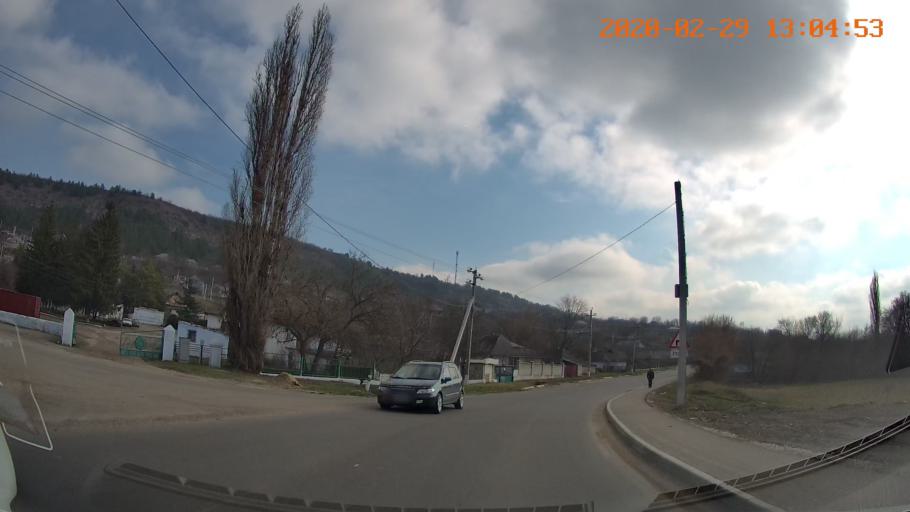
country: MD
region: Telenesti
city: Camenca
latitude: 48.0243
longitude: 28.7077
